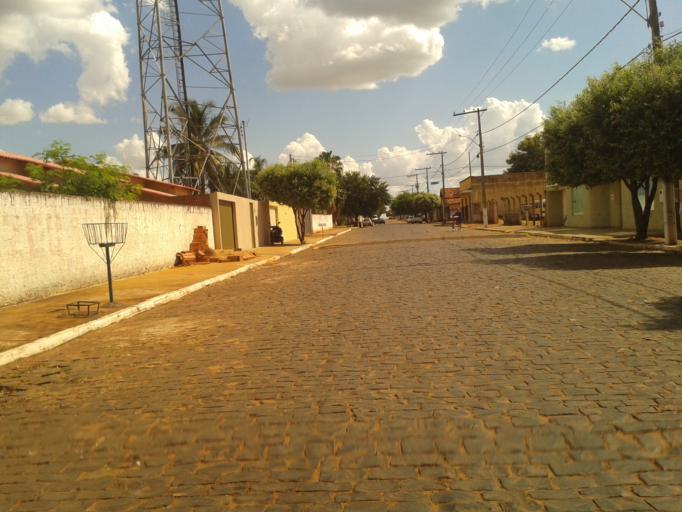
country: BR
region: Minas Gerais
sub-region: Santa Vitoria
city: Santa Vitoria
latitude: -18.6919
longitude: -49.9443
